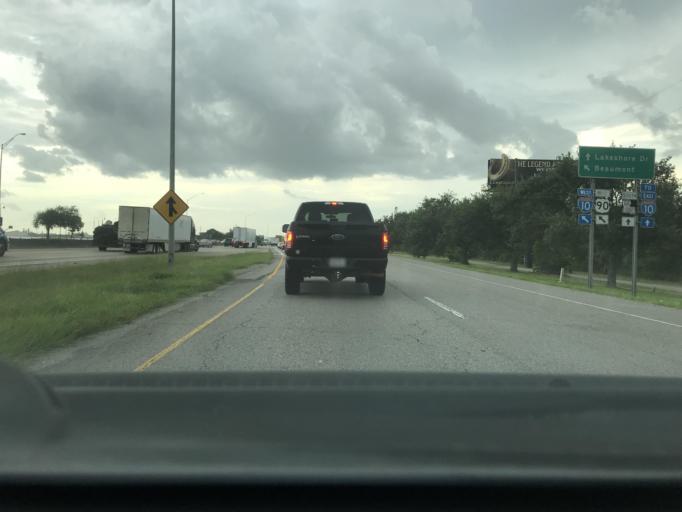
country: US
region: Louisiana
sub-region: Calcasieu Parish
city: Westlake
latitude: 30.2374
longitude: -93.2315
